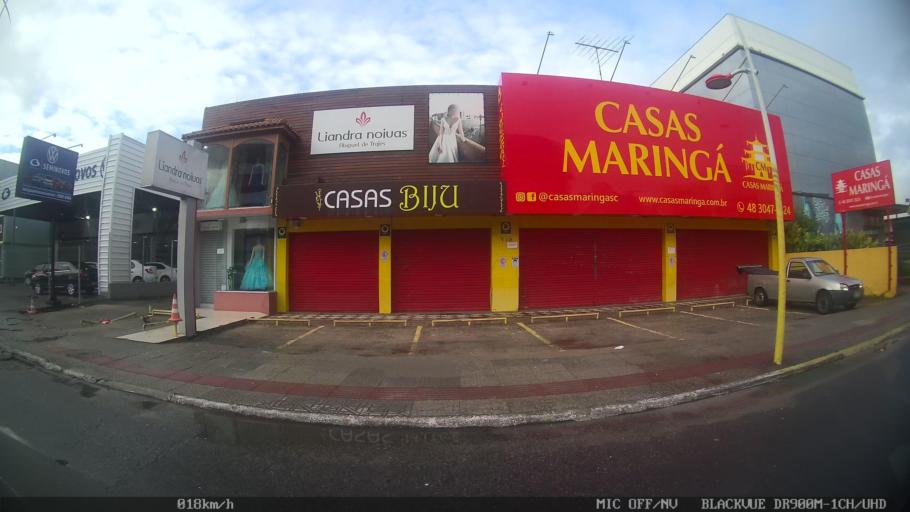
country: BR
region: Santa Catarina
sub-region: Sao Jose
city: Campinas
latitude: -27.6012
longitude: -48.6135
